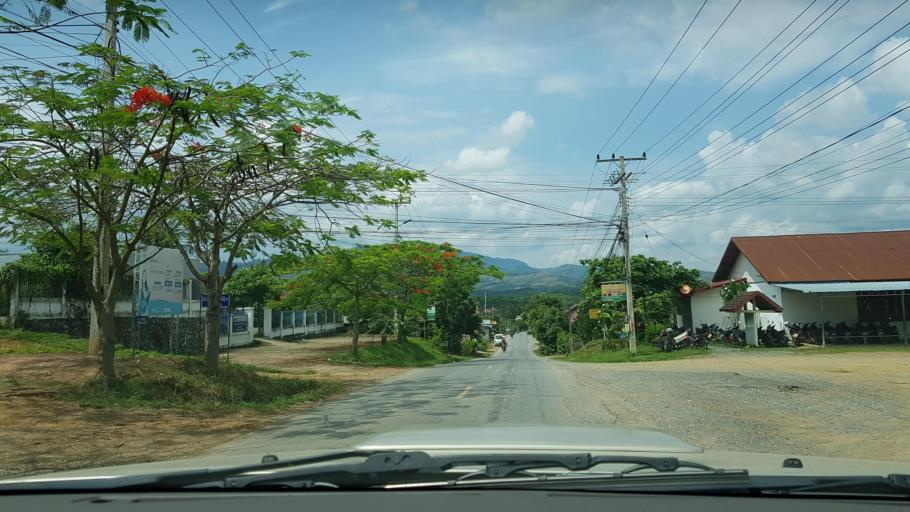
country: LA
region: Loungnamtha
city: Muang Nale
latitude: 20.1415
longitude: 101.4551
